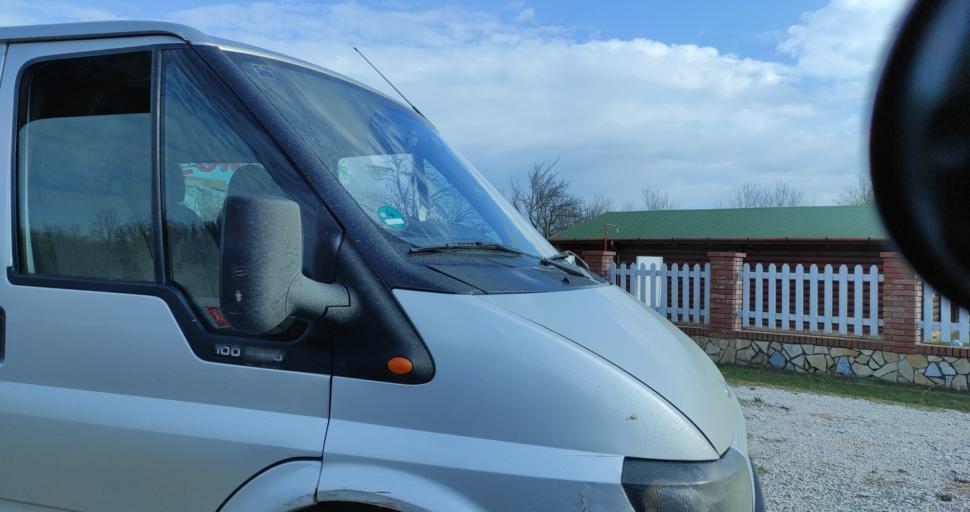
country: AL
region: Lezhe
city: Shengjin
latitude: 41.7790
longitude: 19.6046
